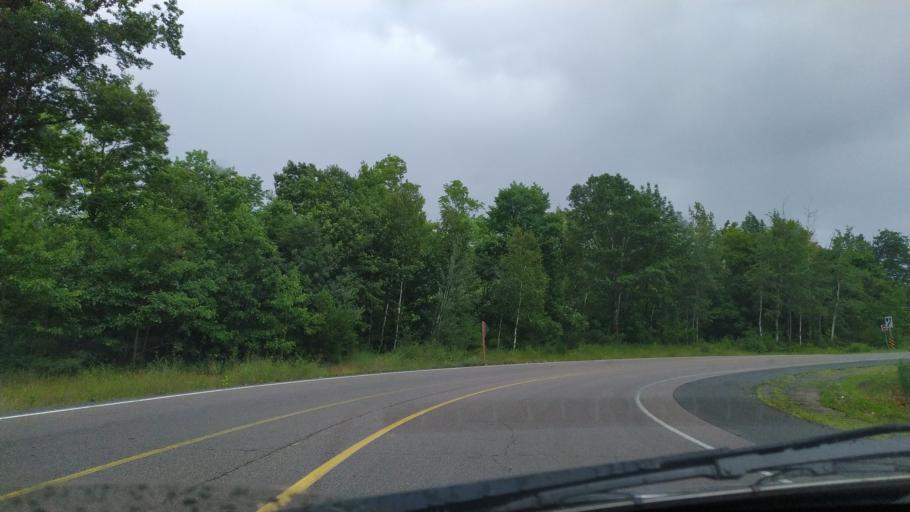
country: CA
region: Ontario
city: Quinte West
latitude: 44.1191
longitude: -77.6280
